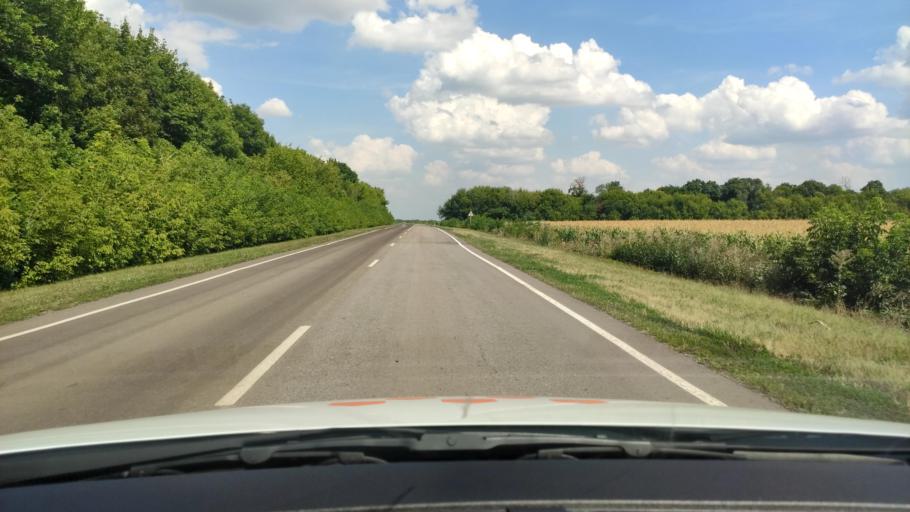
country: RU
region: Voronezj
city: Ertil'
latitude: 51.7975
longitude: 40.7255
